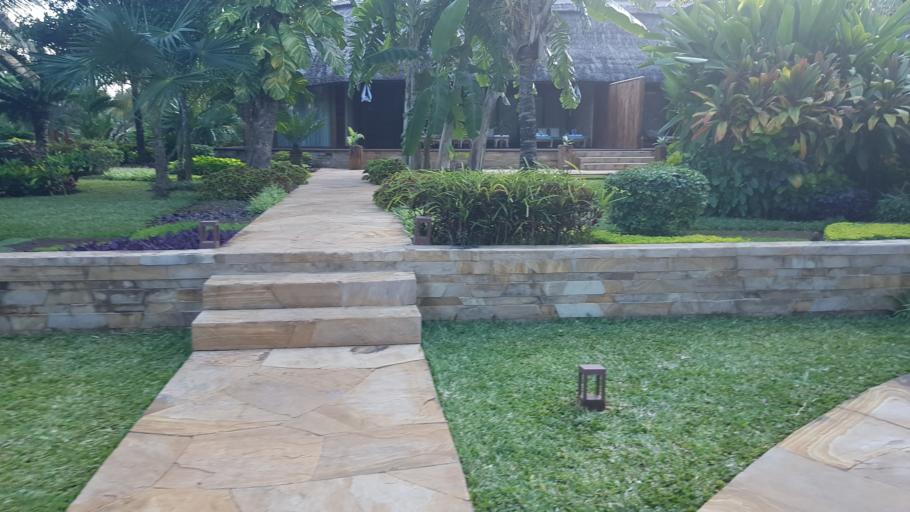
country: TZ
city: Kiwengwa
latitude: -6.0340
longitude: 39.4068
